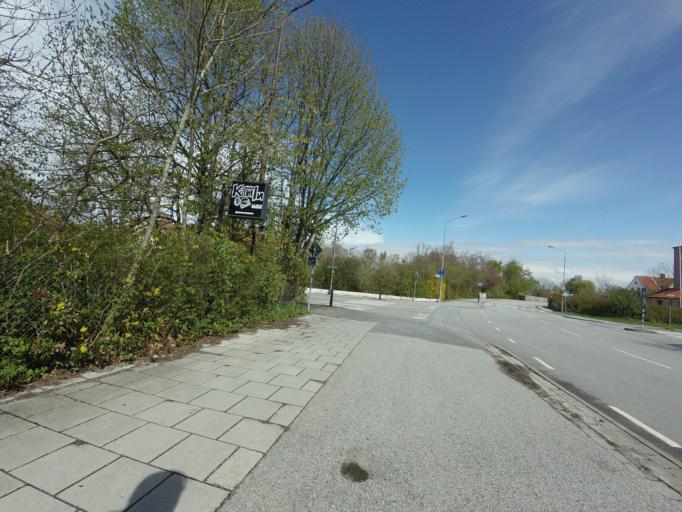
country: SE
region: Skane
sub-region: Malmo
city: Tygelsjo
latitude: 55.5165
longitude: 12.9970
